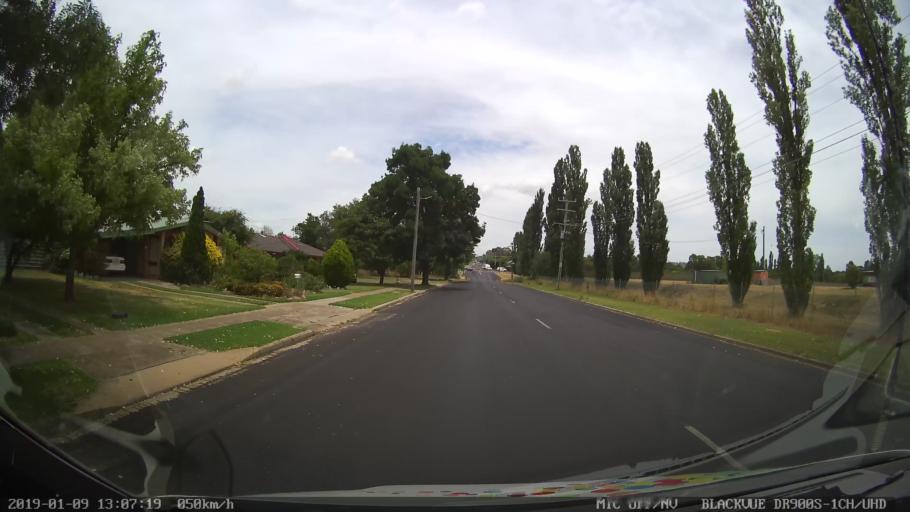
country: AU
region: New South Wales
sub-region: Armidale Dumaresq
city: Armidale
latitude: -30.5188
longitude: 151.6799
